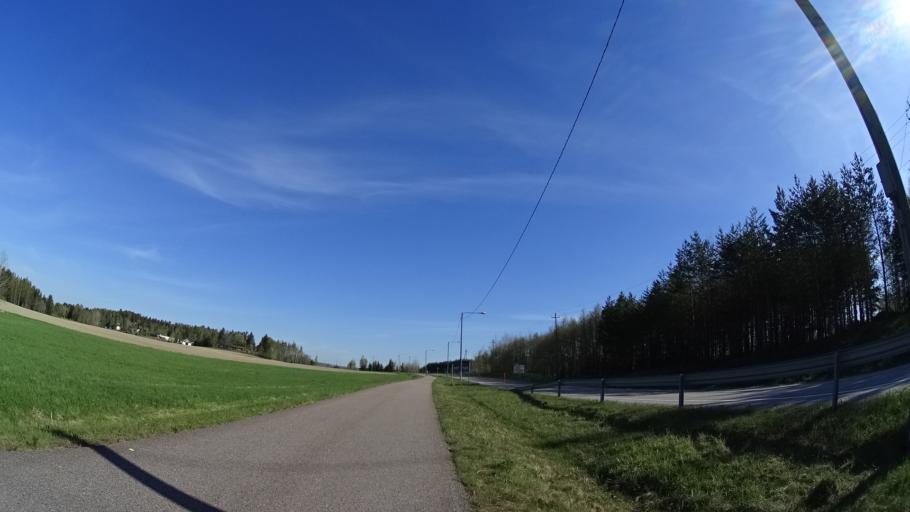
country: FI
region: Uusimaa
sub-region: Helsinki
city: Kilo
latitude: 60.3341
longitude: 24.8178
